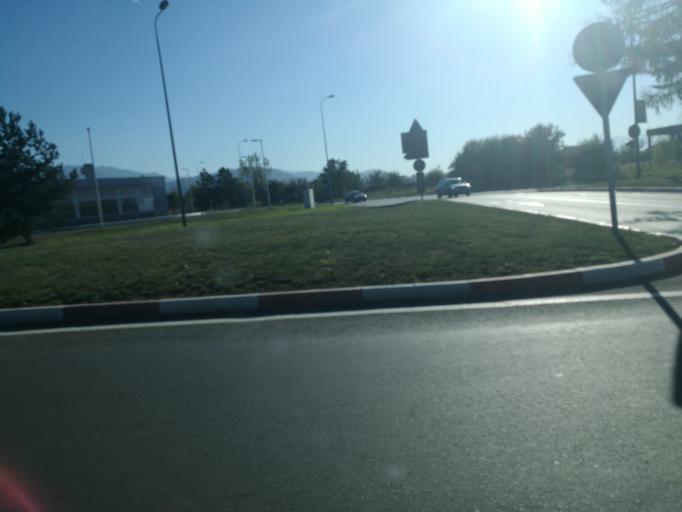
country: RO
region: Brasov
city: Brasov
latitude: 45.6850
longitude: 25.5827
